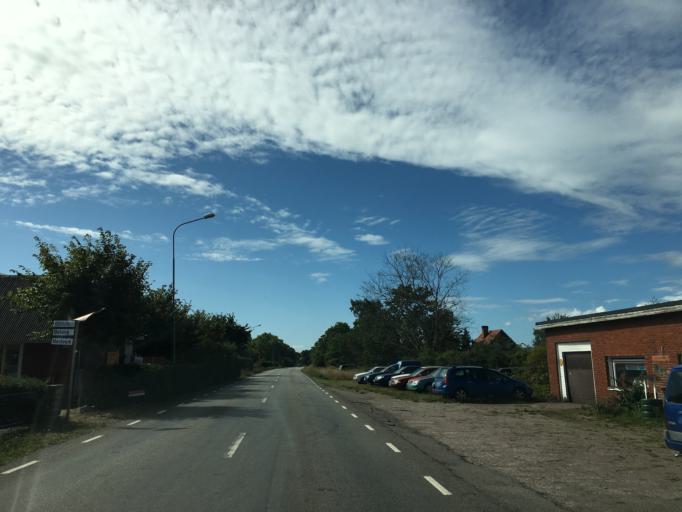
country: SE
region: Kalmar
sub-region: Morbylanga Kommun
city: Moerbylanga
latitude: 56.4492
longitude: 16.4285
